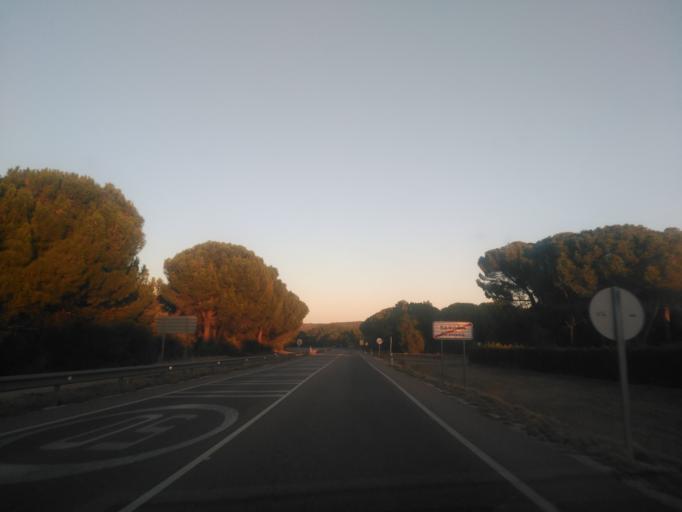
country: ES
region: Castille and Leon
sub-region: Provincia de Valladolid
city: Sardon de Duero
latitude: 41.6072
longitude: -4.4274
